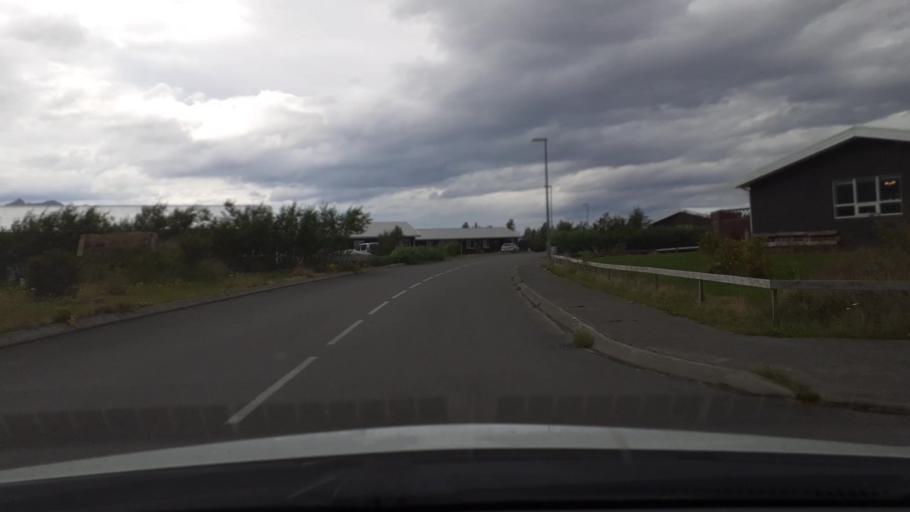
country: IS
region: West
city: Borgarnes
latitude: 64.5617
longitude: -21.7576
